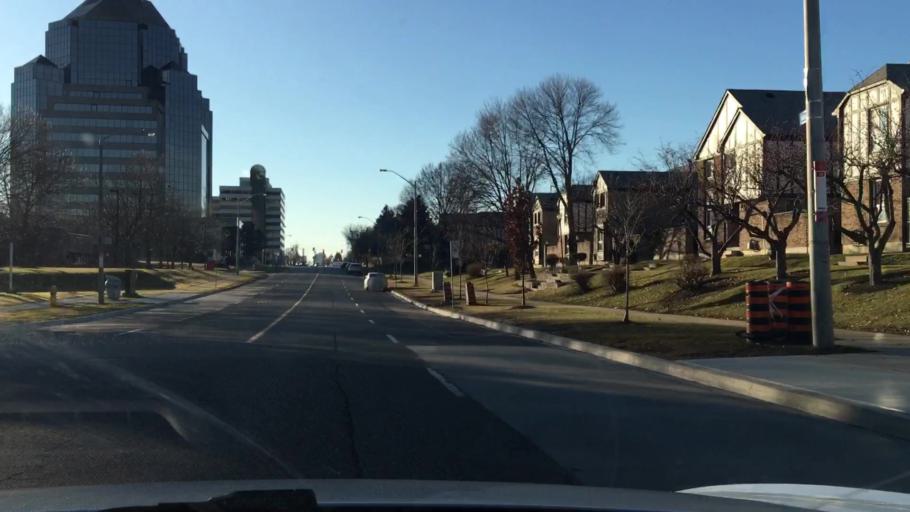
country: CA
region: Ontario
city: Scarborough
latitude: 43.7910
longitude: -79.2305
